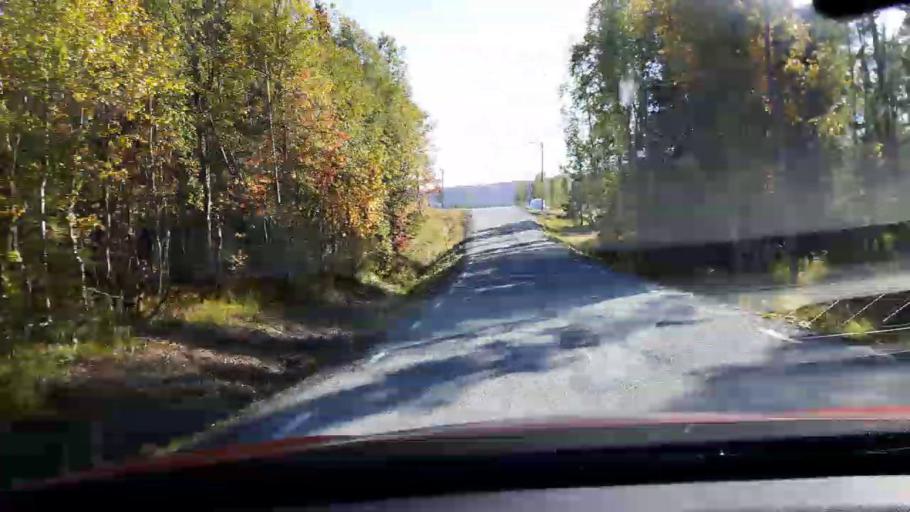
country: NO
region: Nord-Trondelag
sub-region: Royrvik
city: Royrvik
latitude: 64.8174
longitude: 14.1445
